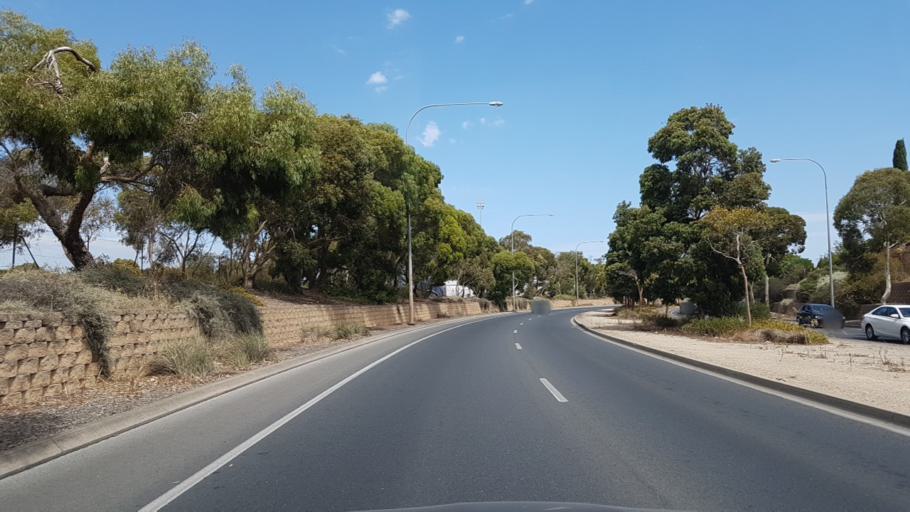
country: AU
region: South Australia
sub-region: City of West Torrens
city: Thebarton
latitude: -34.9269
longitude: 138.5793
